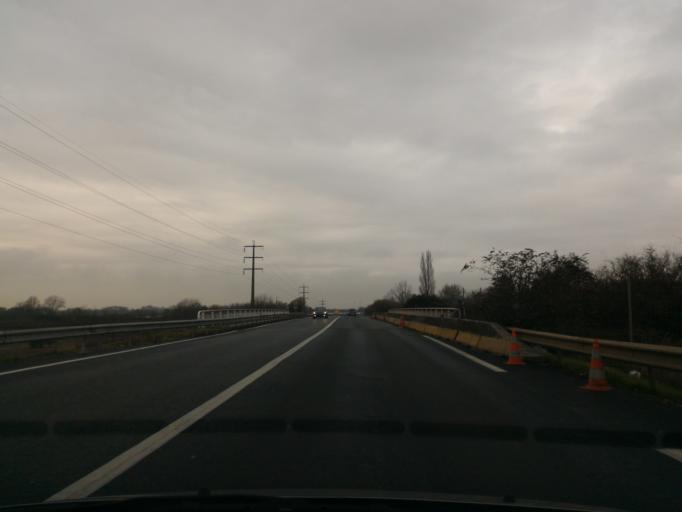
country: FR
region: Poitou-Charentes
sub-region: Departement de la Vienne
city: Biard
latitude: 46.5453
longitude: 0.2970
